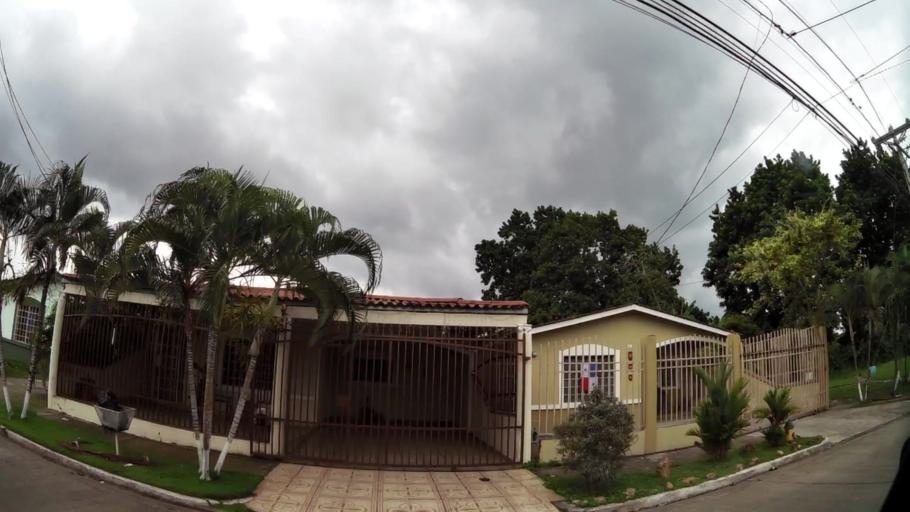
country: PA
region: Panama
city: Tocumen
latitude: 9.0478
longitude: -79.4041
